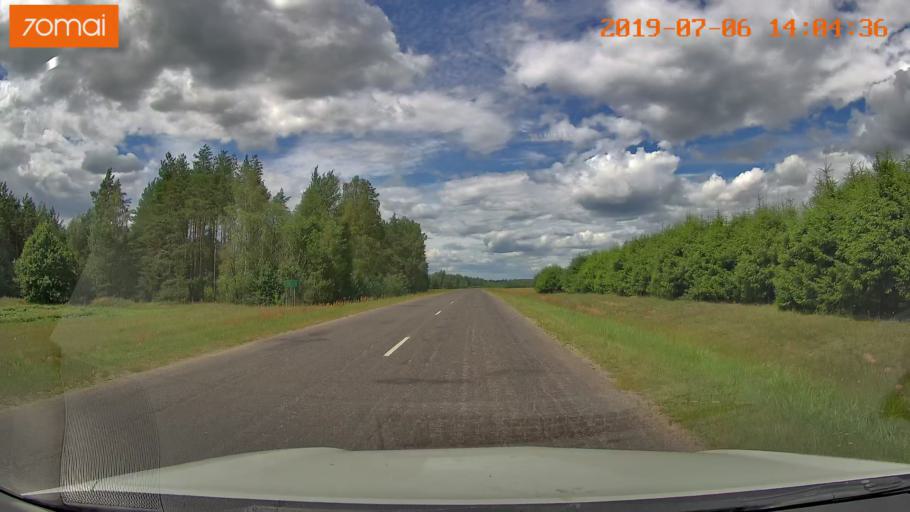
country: BY
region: Minsk
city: Ivyanyets
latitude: 53.8416
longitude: 26.7978
